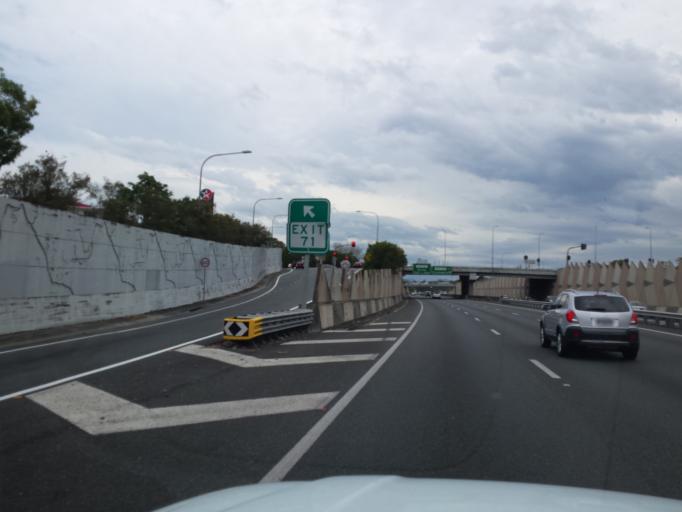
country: AU
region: Queensland
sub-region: Gold Coast
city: Nerang
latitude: -27.9920
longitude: 153.3404
